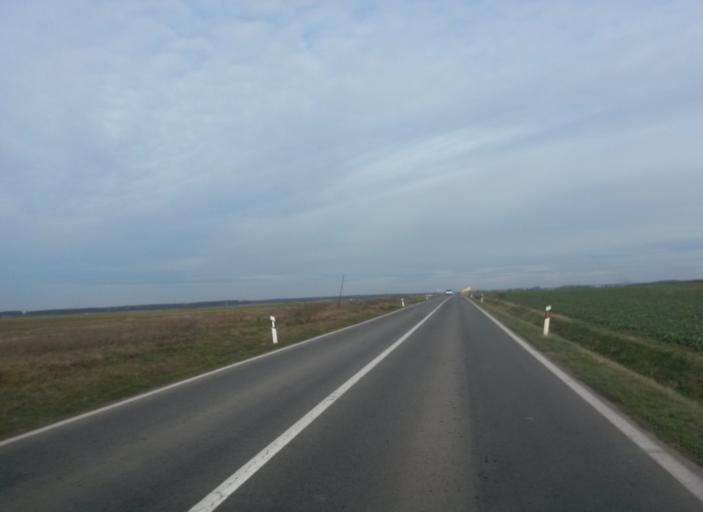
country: HR
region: Osjecko-Baranjska
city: Viskovci
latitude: 45.3758
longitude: 18.4397
